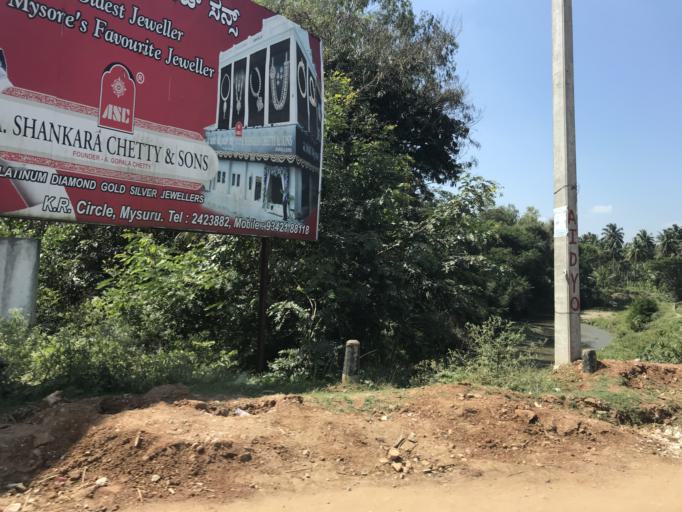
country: IN
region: Karnataka
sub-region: Mysore
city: Heggadadevankote
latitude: 12.0847
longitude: 76.3344
